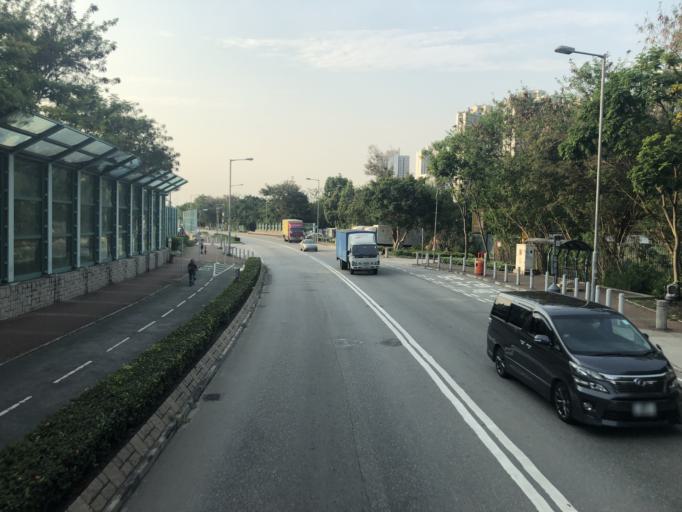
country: HK
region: Yuen Long
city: Yuen Long Kau Hui
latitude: 22.4523
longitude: 113.9949
